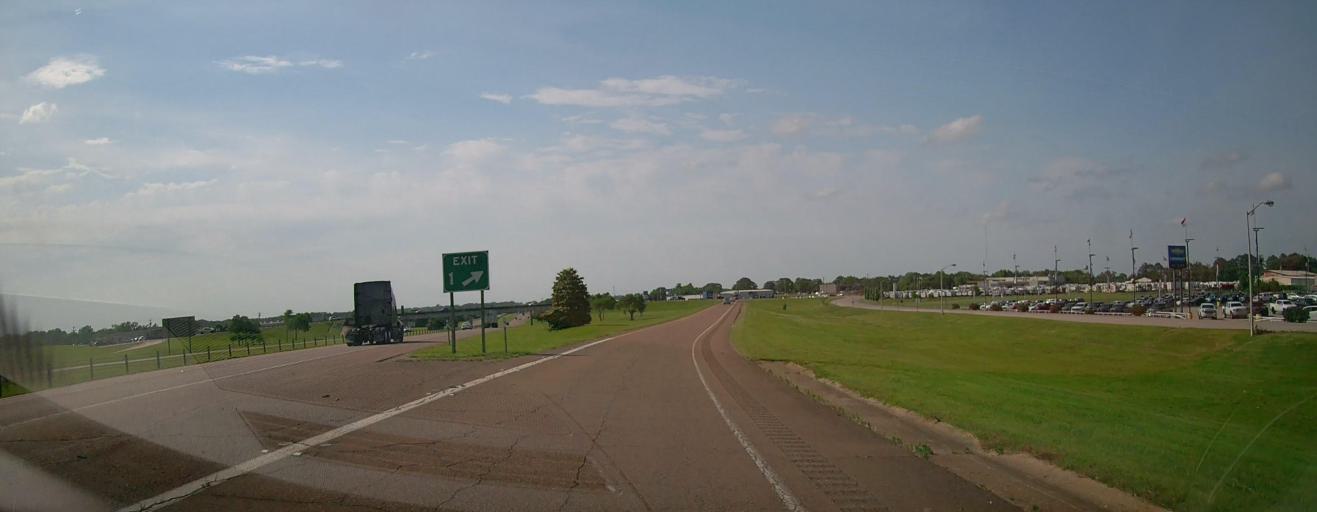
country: US
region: Mississippi
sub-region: De Soto County
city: Olive Branch
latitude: 34.9743
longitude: -89.8625
